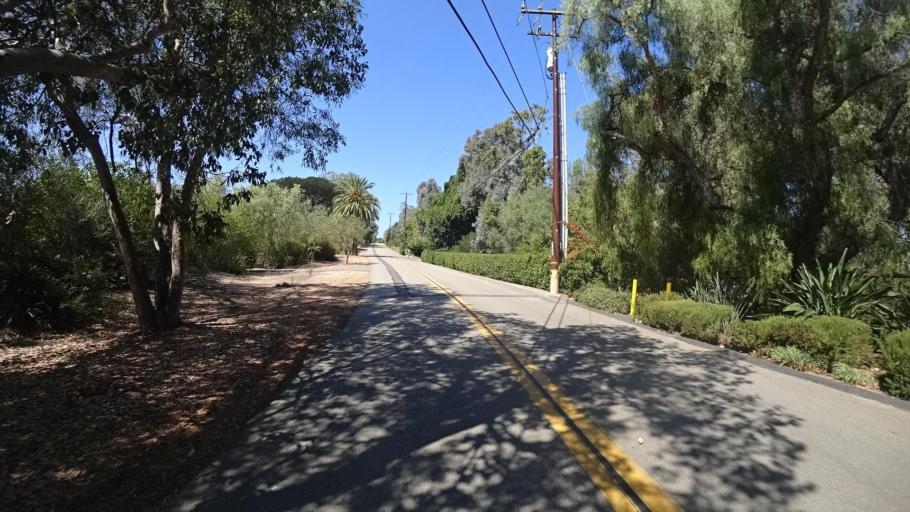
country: US
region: California
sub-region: San Diego County
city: Rancho Santa Fe
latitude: 33.0206
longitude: -117.1827
